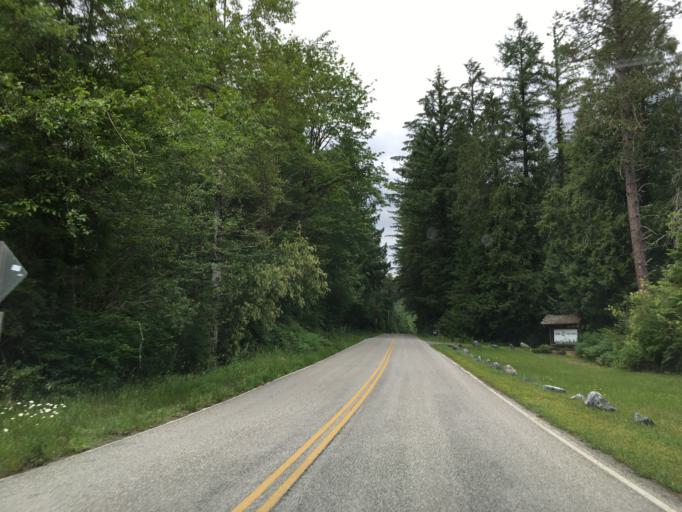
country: US
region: Washington
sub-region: Whatcom County
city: Peaceful Valley
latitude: 48.9842
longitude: -122.0753
